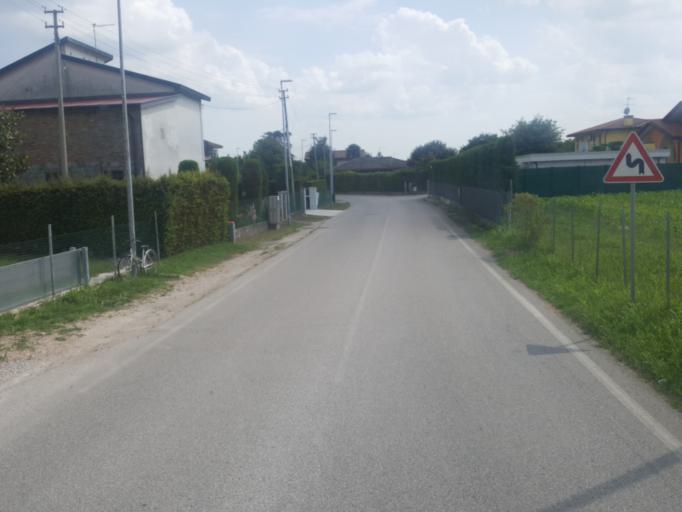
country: IT
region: Veneto
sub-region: Provincia di Padova
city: Vallonga
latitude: 45.2766
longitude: 12.0891
